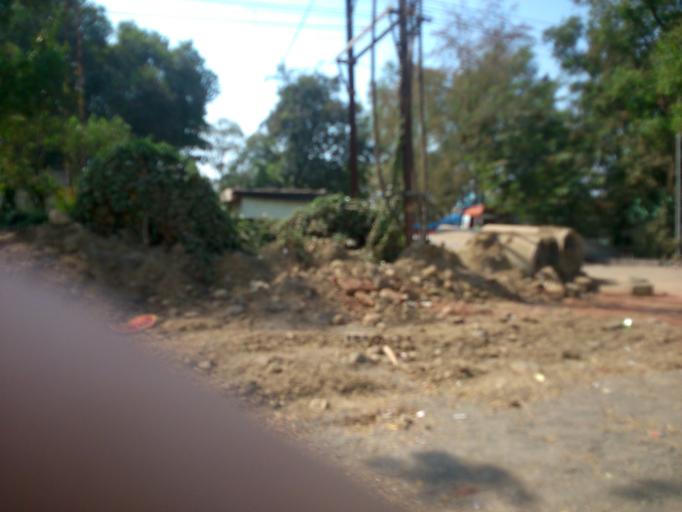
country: IN
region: Maharashtra
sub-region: Thane
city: Amarnath
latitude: 19.2182
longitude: 73.1772
